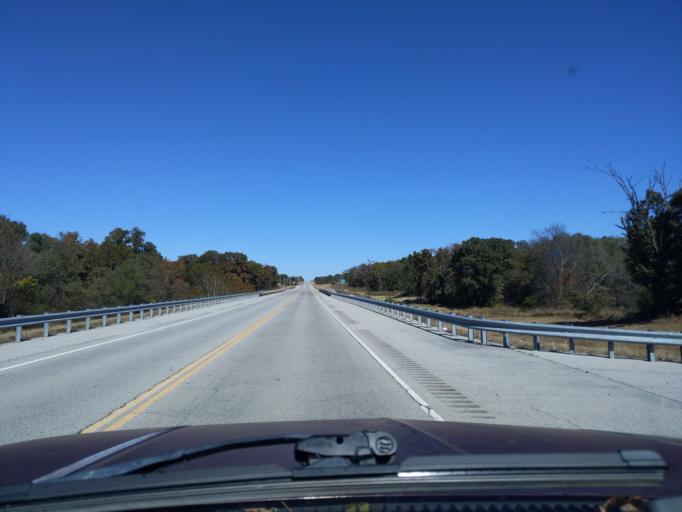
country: US
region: Oklahoma
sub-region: Creek County
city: Bristow
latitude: 35.7345
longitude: -96.3873
